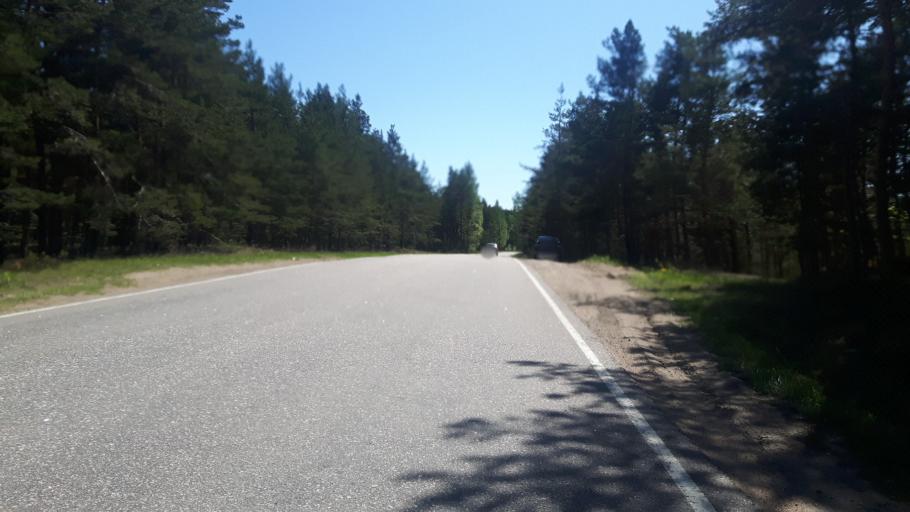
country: RU
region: Leningrad
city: Glebychevo
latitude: 60.3322
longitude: 28.8213
